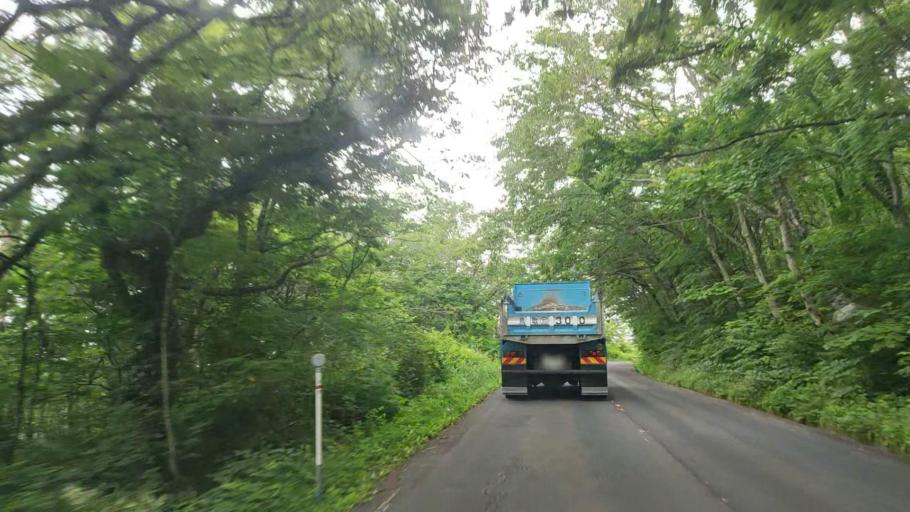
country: JP
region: Tottori
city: Yonago
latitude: 35.3749
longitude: 133.5181
